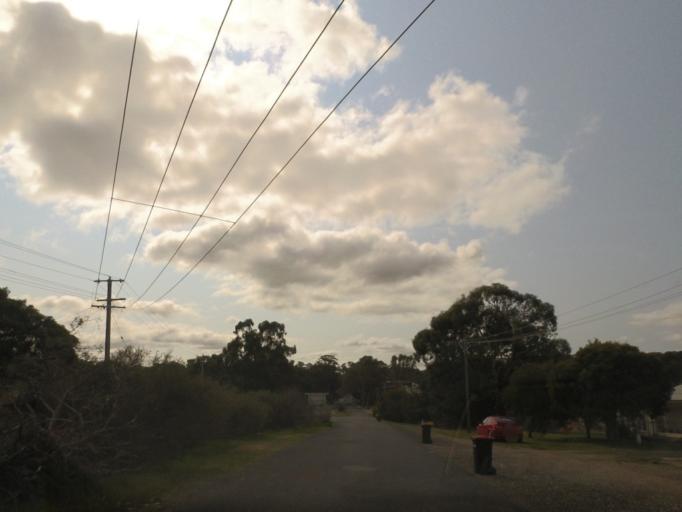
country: AU
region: Victoria
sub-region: Murrindindi
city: Kinglake West
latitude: -37.0933
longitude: 145.1037
